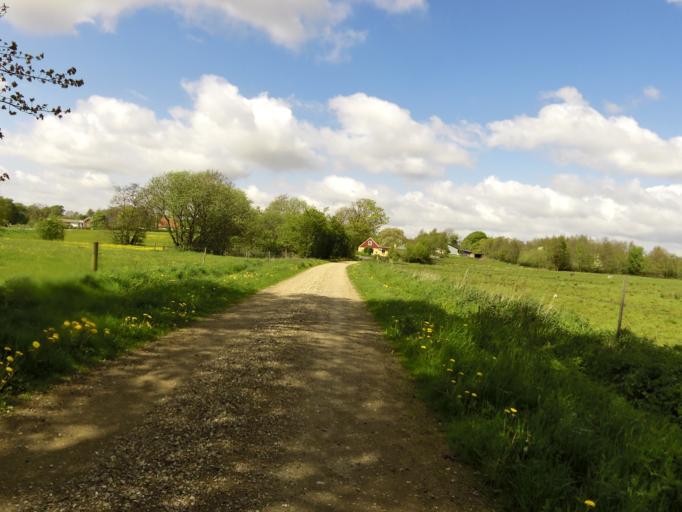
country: DK
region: South Denmark
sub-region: Haderslev Kommune
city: Gram
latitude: 55.3265
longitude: 9.0605
